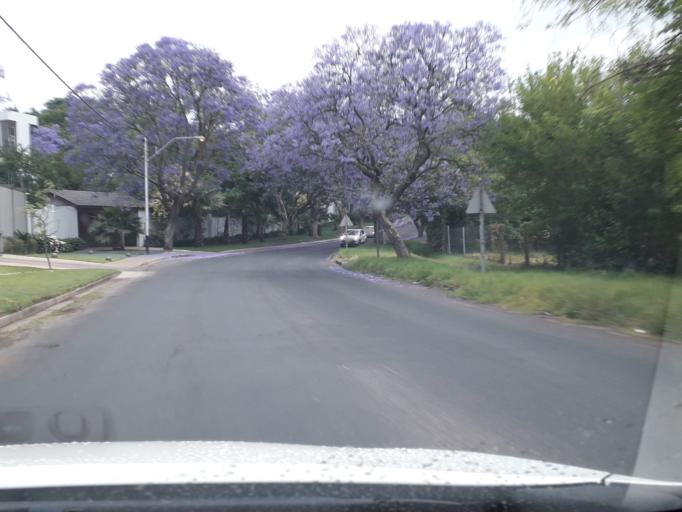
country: ZA
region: Gauteng
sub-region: City of Johannesburg Metropolitan Municipality
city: Johannesburg
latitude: -26.1441
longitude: 28.0502
